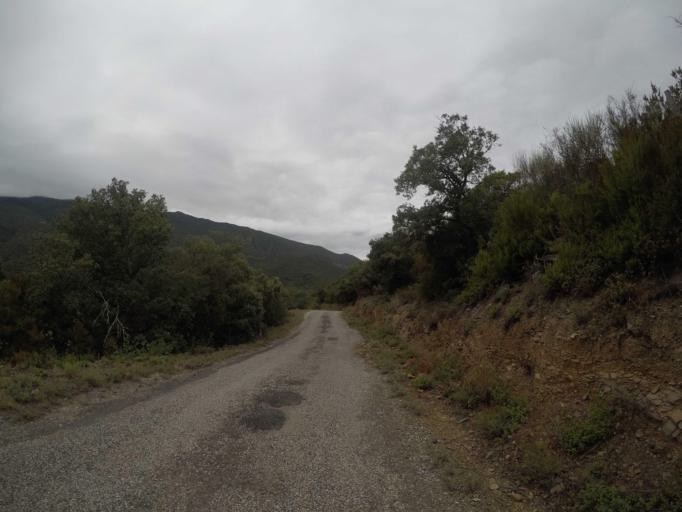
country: FR
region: Languedoc-Roussillon
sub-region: Departement des Pyrenees-Orientales
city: Ille-sur-Tet
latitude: 42.6121
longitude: 2.6109
